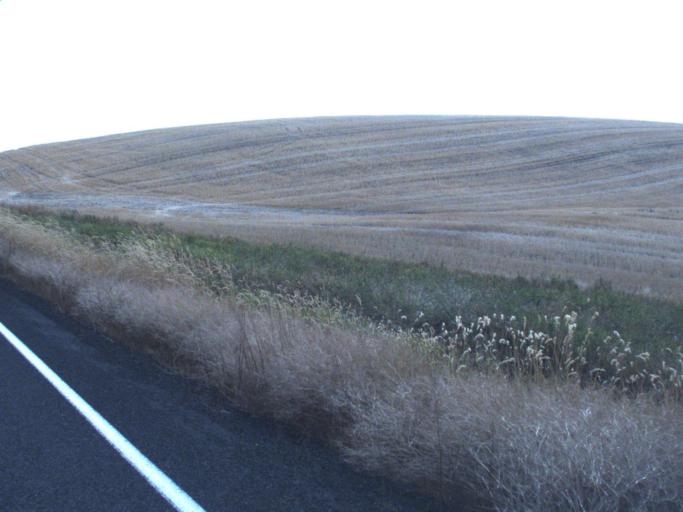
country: US
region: Washington
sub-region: Lincoln County
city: Davenport
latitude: 47.4767
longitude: -117.9512
